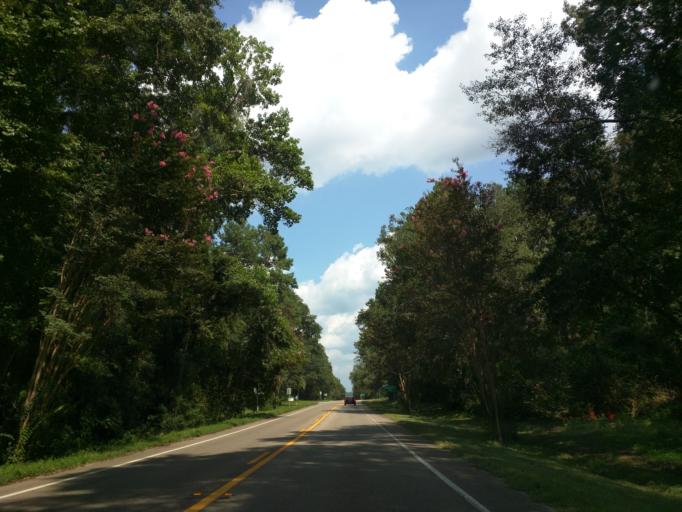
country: US
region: Florida
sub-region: Jefferson County
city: Monticello
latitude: 30.5208
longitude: -84.0557
